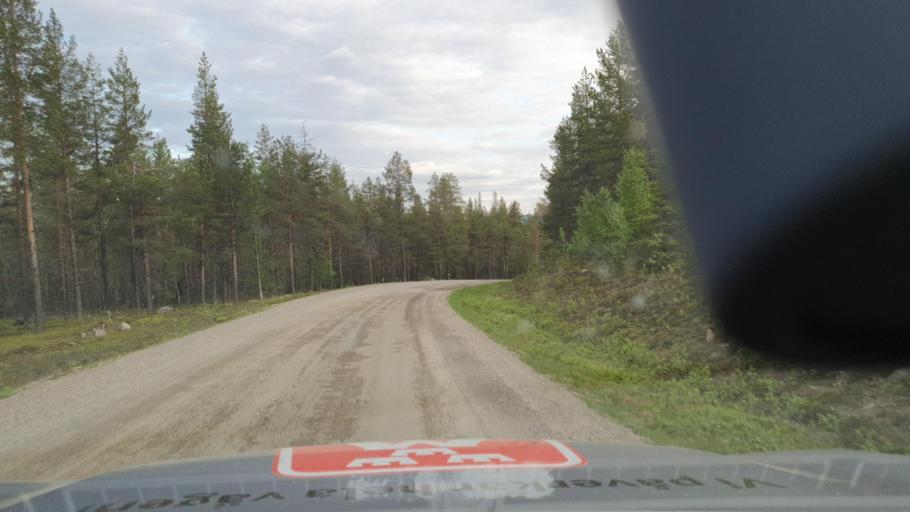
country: SE
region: Norrbotten
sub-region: Gallivare Kommun
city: Gaellivare
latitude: 66.7004
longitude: 21.1665
